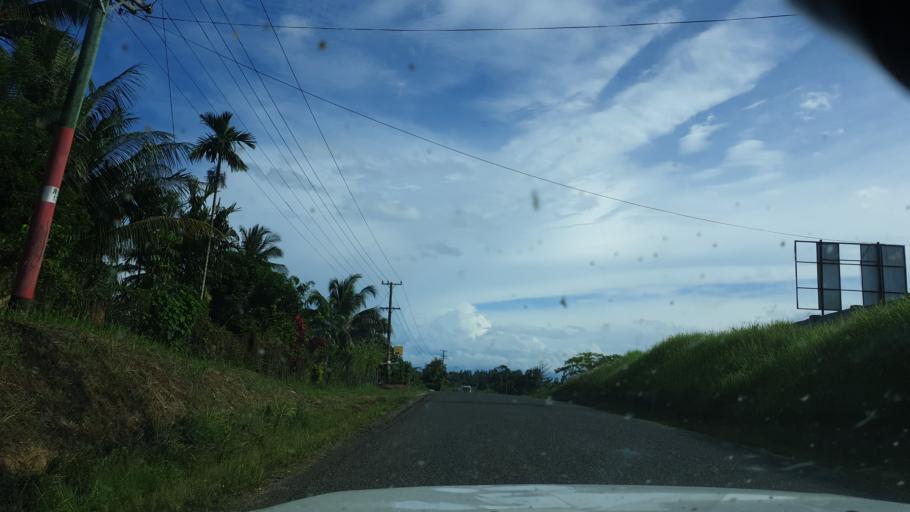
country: PG
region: Madang
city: Madang
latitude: -5.2070
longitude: 145.7737
